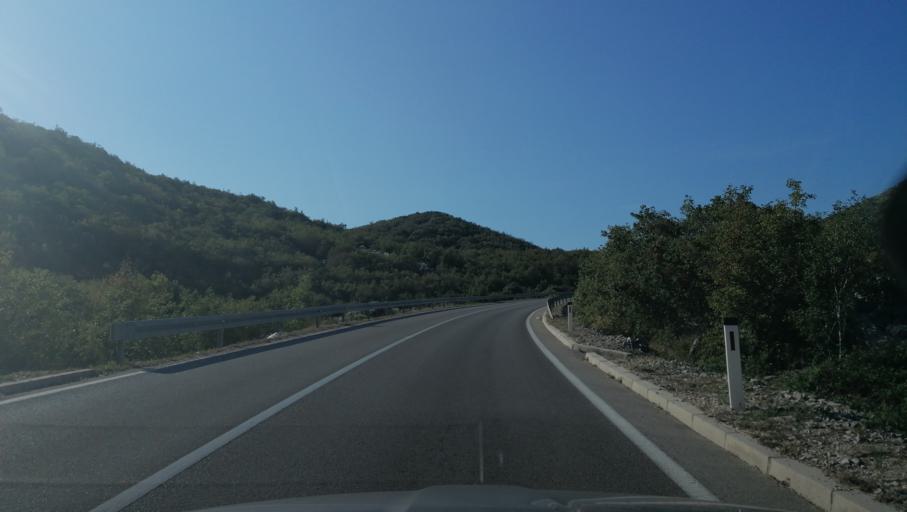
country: BA
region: Republika Srpska
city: Trebinje
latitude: 42.6580
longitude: 18.3665
